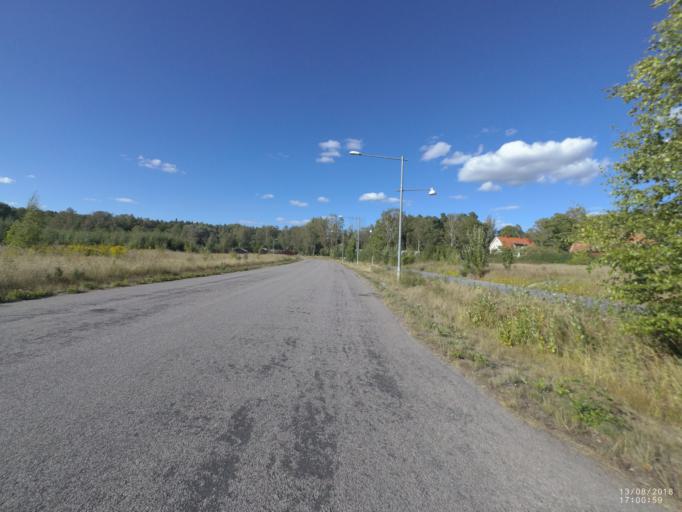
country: SE
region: Soedermanland
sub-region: Nykopings Kommun
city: Nykoping
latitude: 58.7549
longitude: 16.9774
